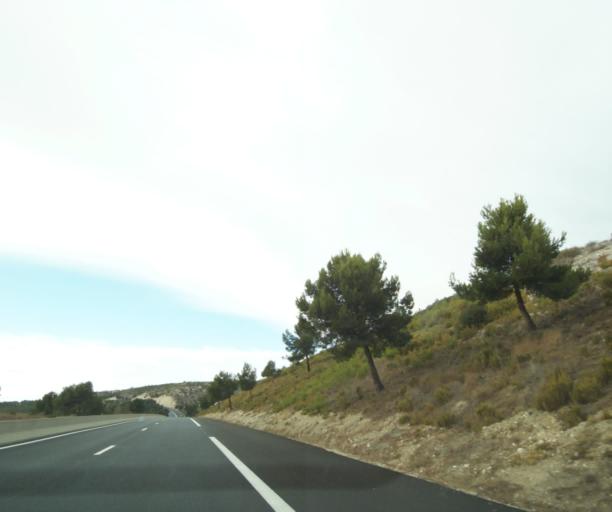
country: FR
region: Provence-Alpes-Cote d'Azur
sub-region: Departement des Bouches-du-Rhone
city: Carry-le-Rouet
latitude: 43.3404
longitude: 5.1348
